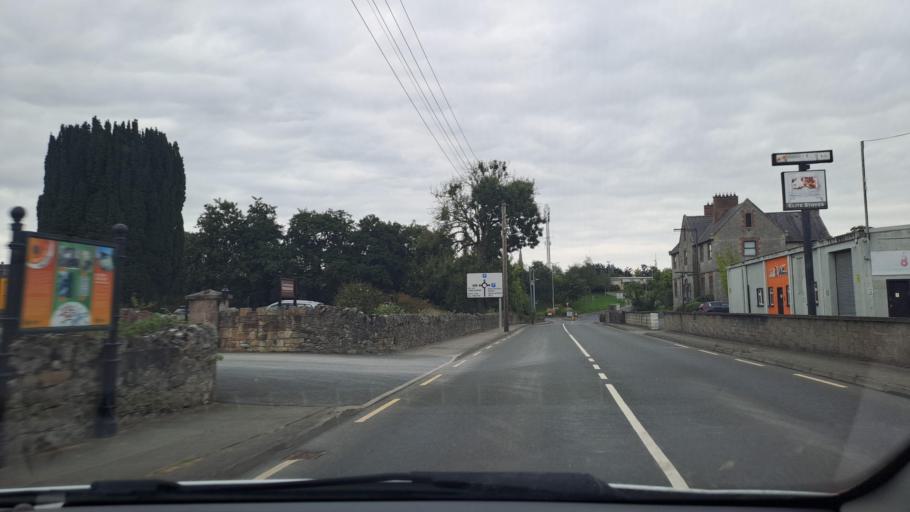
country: IE
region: Ulster
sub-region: County Monaghan
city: Carrickmacross
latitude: 53.9783
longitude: -6.7256
